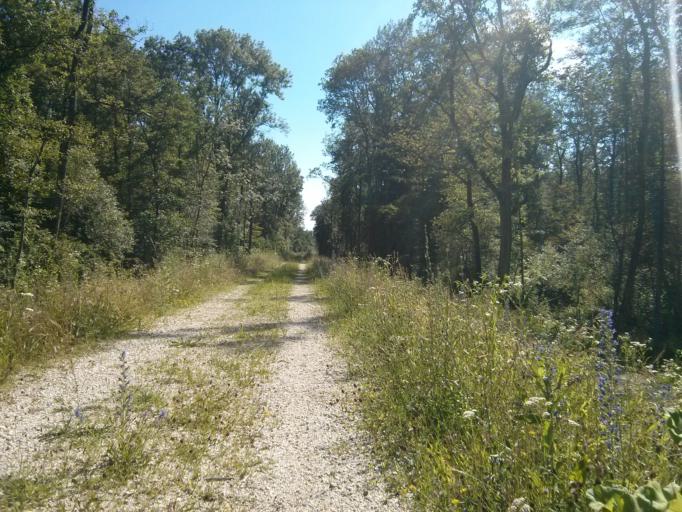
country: DE
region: Bavaria
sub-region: Lower Bavaria
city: Moos
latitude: 48.7924
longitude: 12.9499
